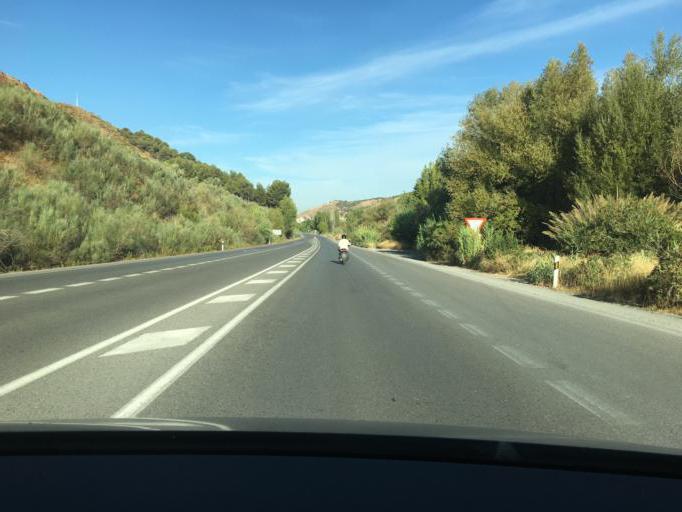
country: ES
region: Andalusia
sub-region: Provincia de Granada
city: Cenes de la Vega
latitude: 37.1566
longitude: -3.5469
